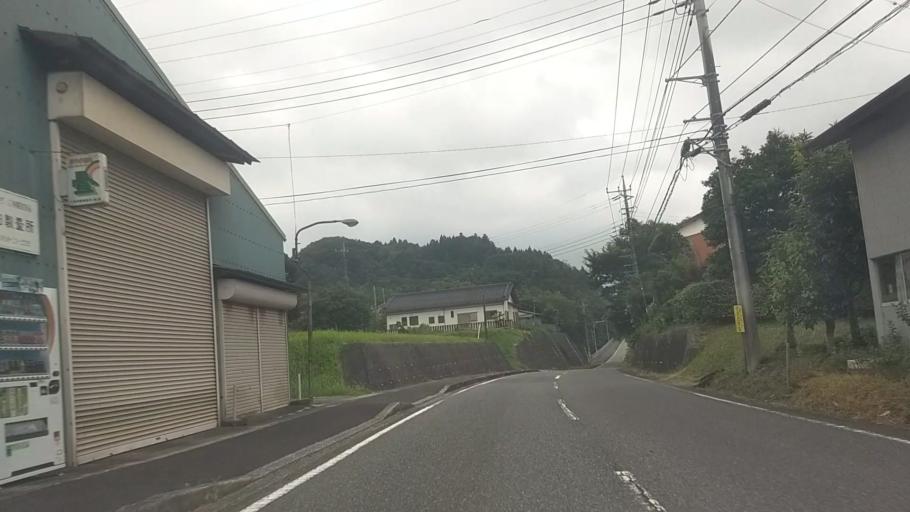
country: JP
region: Chiba
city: Kawaguchi
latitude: 35.2442
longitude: 140.0821
